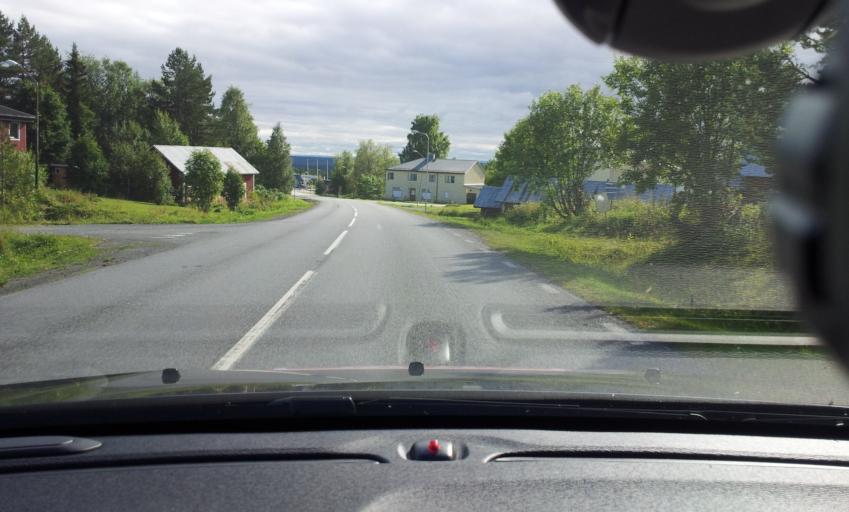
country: SE
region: Jaemtland
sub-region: Krokoms Kommun
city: Krokom
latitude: 63.4578
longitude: 14.1899
